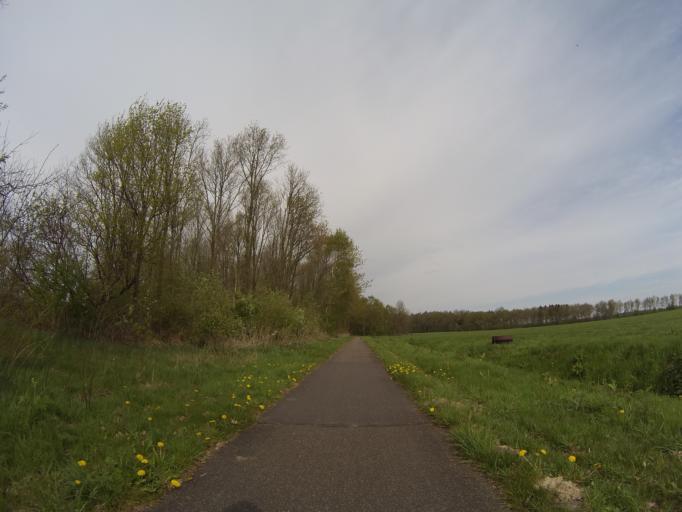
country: NL
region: Drenthe
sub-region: Gemeente Coevorden
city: Sleen
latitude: 52.8341
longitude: 6.6810
